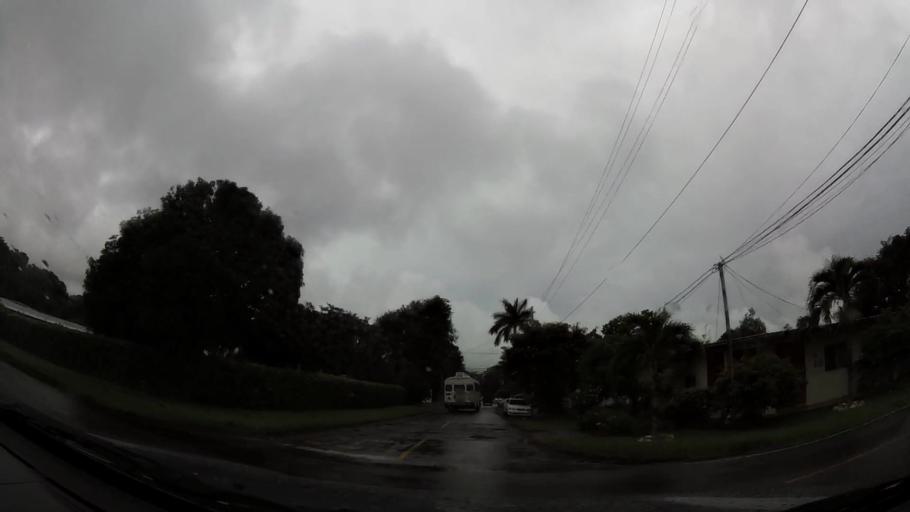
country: PA
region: Chiriqui
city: David
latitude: 8.4320
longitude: -82.4396
